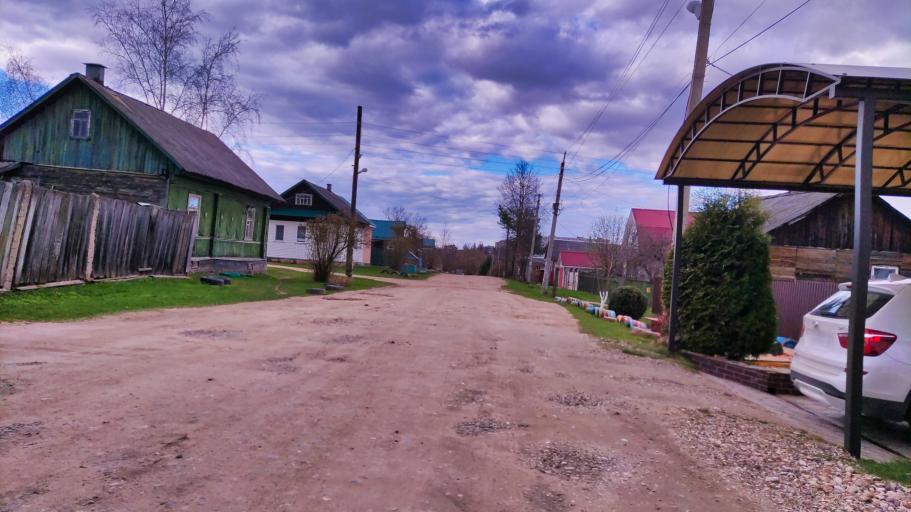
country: RU
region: Tverskaya
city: Rzhev
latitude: 56.2501
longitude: 34.3434
